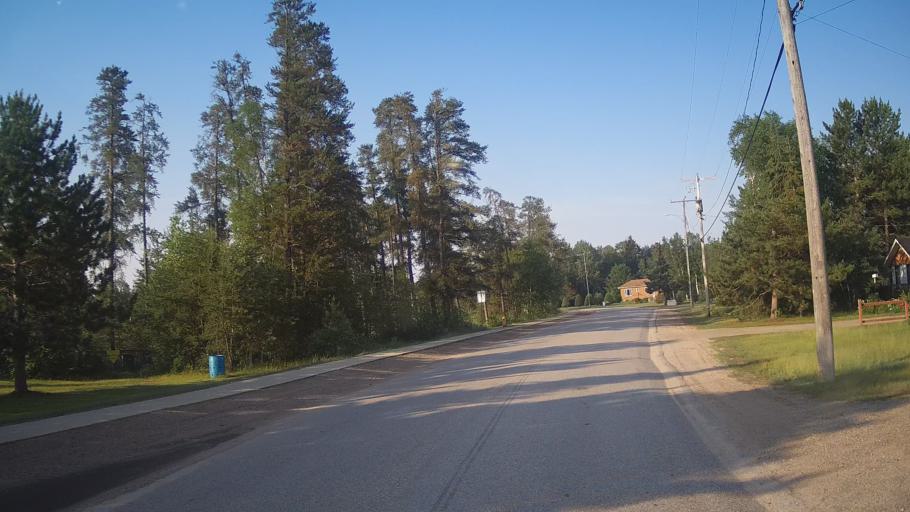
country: CA
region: Ontario
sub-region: Rainy River District
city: Atikokan
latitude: 49.4093
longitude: -91.6575
